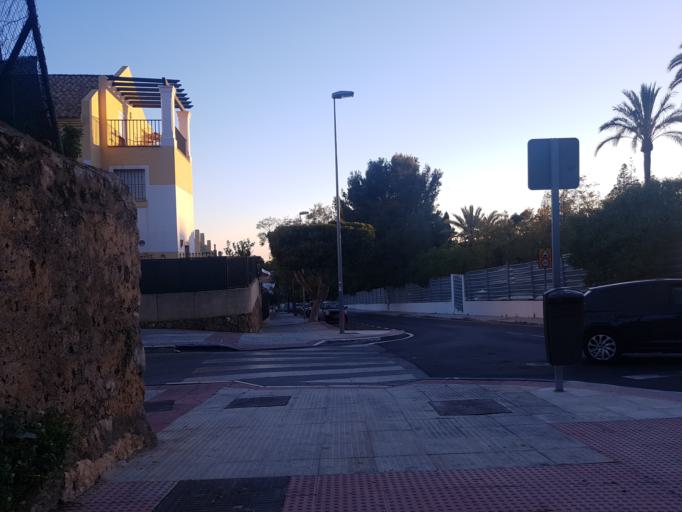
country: ES
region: Andalusia
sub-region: Provincia de Malaga
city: Marbella
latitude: 36.5248
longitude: -4.8912
